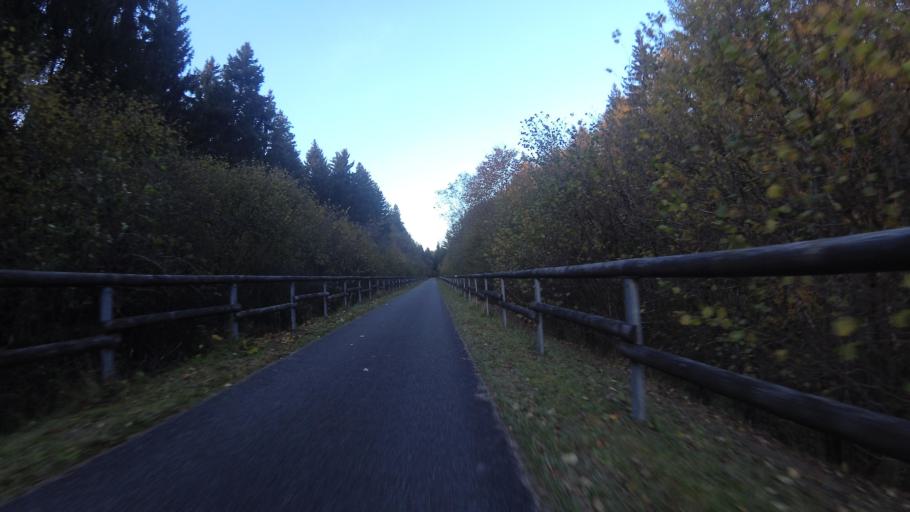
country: DE
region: Rheinland-Pfalz
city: Kell
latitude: 49.6534
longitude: 6.8467
